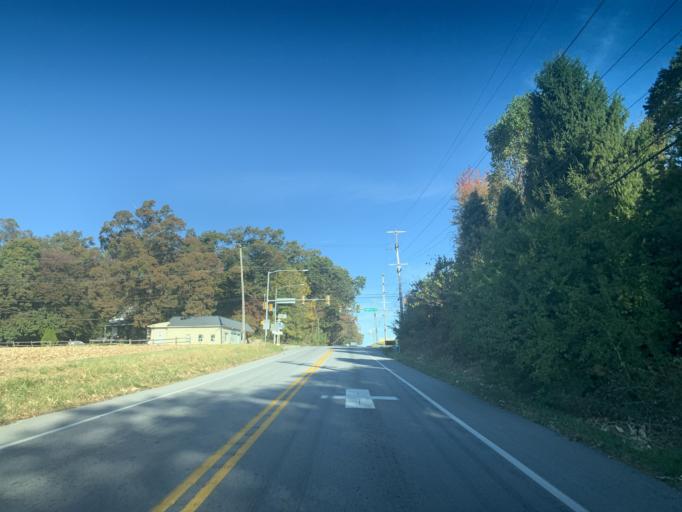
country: US
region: Pennsylvania
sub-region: Chester County
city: Parkesburg
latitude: 39.9383
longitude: -75.9105
